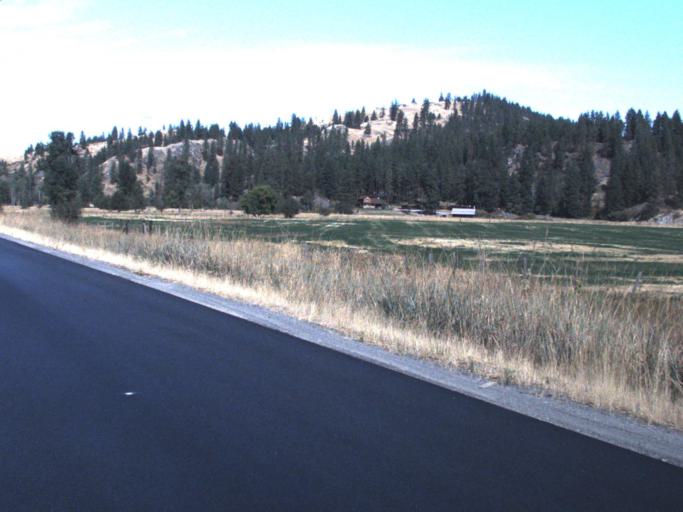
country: US
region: Washington
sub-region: Stevens County
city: Colville
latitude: 48.4728
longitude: -117.8918
